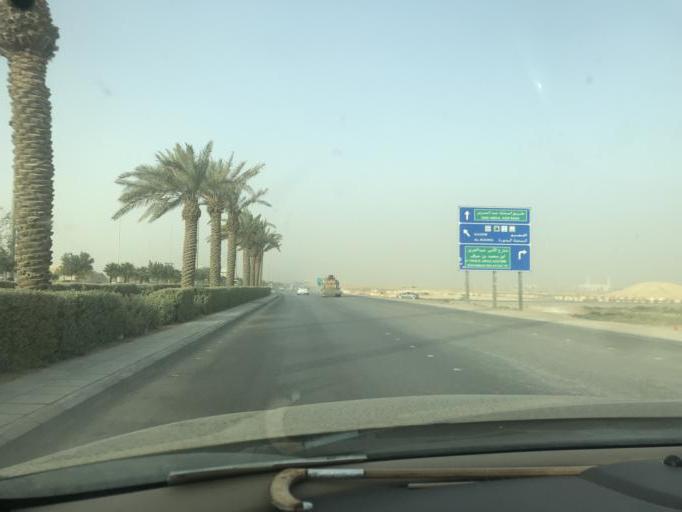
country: SA
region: Ar Riyad
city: Riyadh
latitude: 24.8395
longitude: 46.6442
